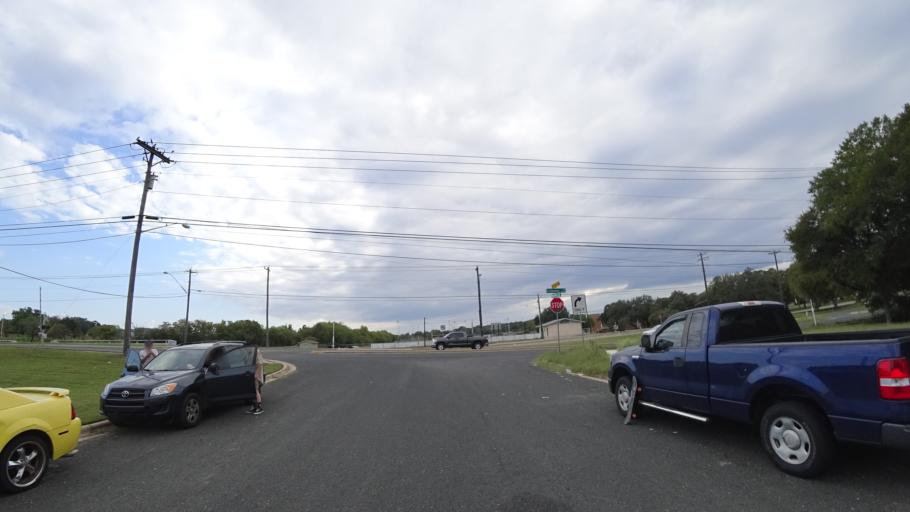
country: US
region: Texas
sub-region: Travis County
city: Rollingwood
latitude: 30.2140
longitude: -97.7941
